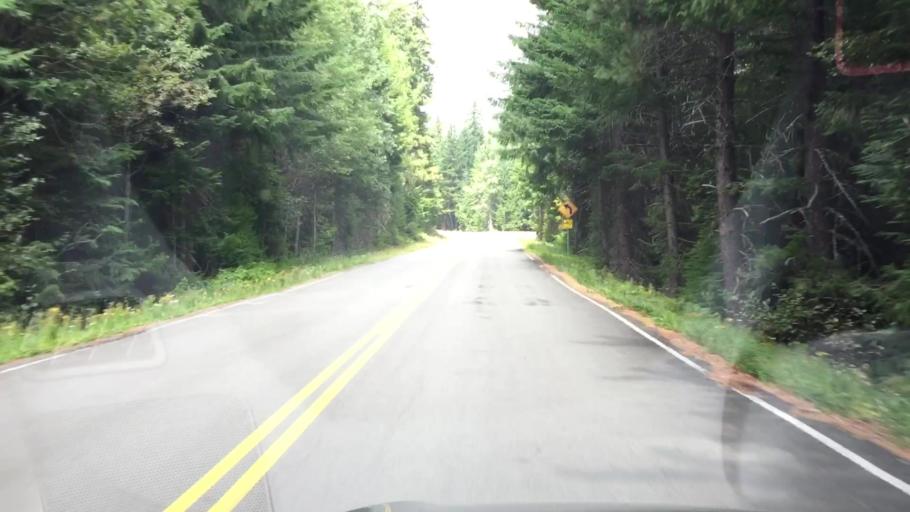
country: US
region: Washington
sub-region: Klickitat County
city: White Salmon
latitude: 46.1142
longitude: -121.6160
